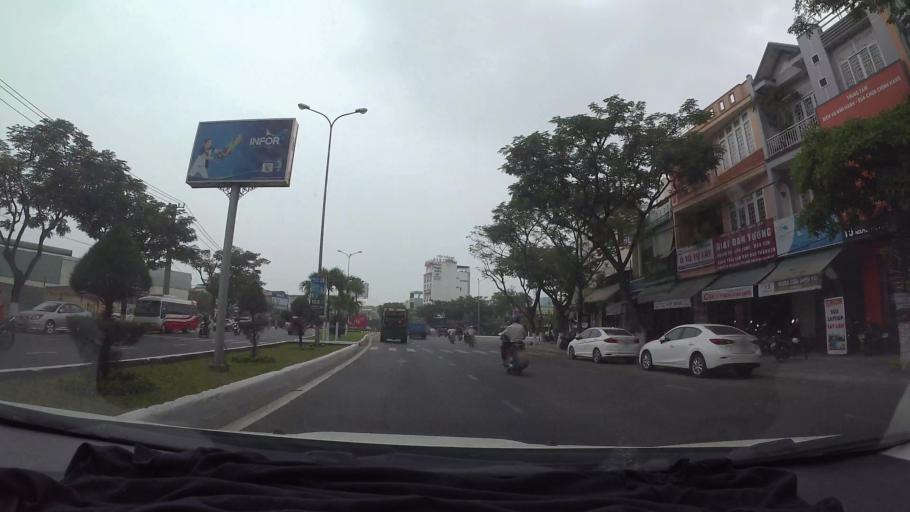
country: VN
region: Da Nang
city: Da Nang
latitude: 16.0558
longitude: 108.2082
